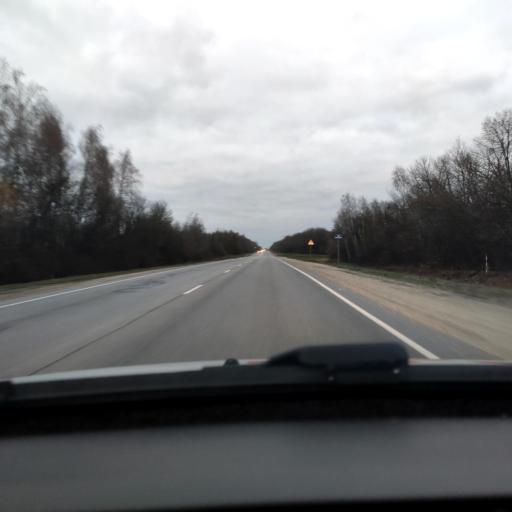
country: RU
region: Lipetsk
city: Khlevnoye
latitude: 52.3366
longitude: 39.1809
